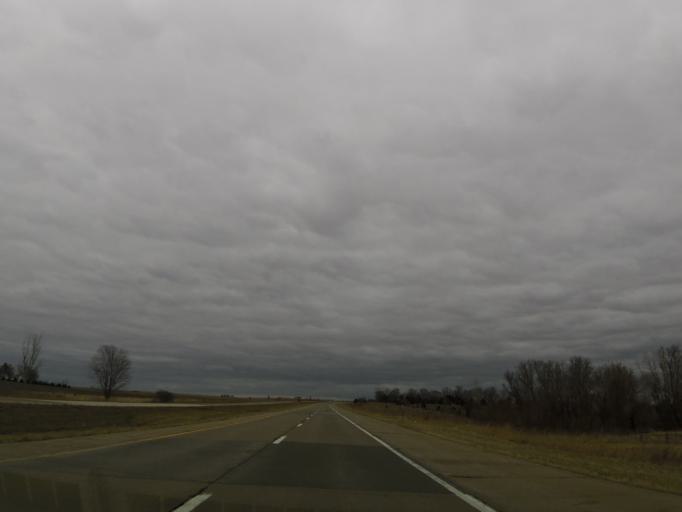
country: US
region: Iowa
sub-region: Benton County
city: Urbana
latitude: 42.2783
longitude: -91.9352
